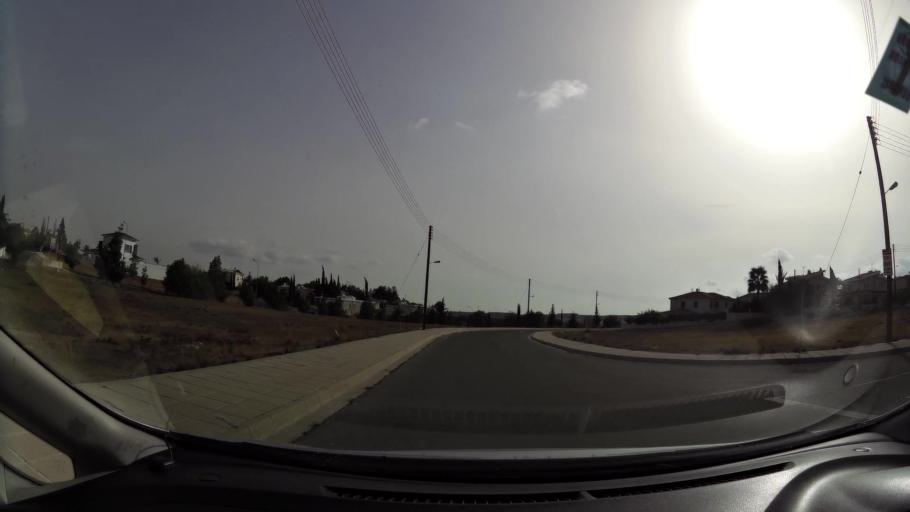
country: CY
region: Lefkosia
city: Geri
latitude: 35.0795
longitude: 33.3896
